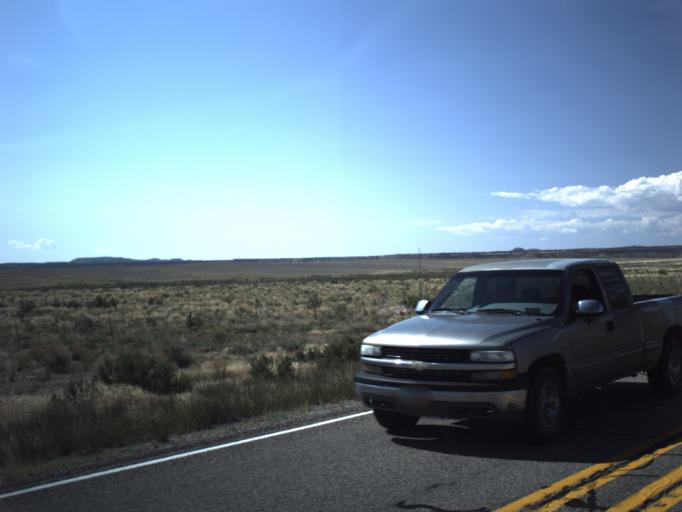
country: US
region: Utah
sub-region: Emery County
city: Ferron
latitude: 38.8474
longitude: -111.3104
